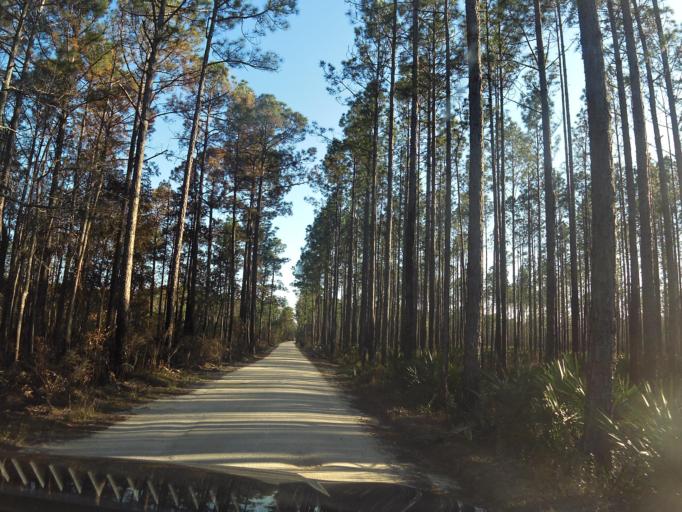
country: US
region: Florida
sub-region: Clay County
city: Middleburg
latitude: 30.1499
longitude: -81.8822
